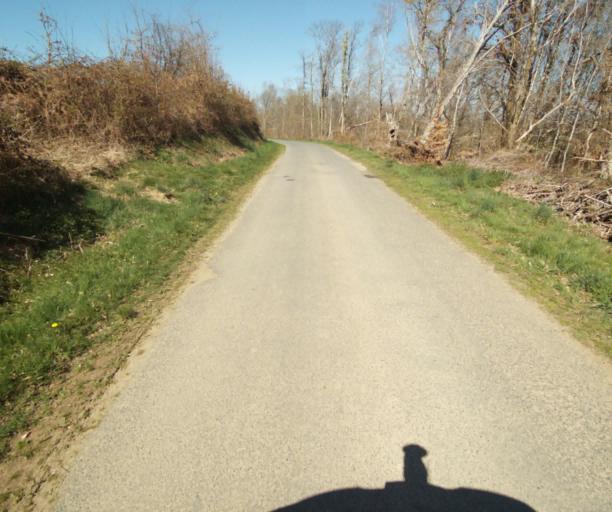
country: FR
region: Limousin
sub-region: Departement de la Correze
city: Chamboulive
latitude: 45.4416
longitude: 1.6830
